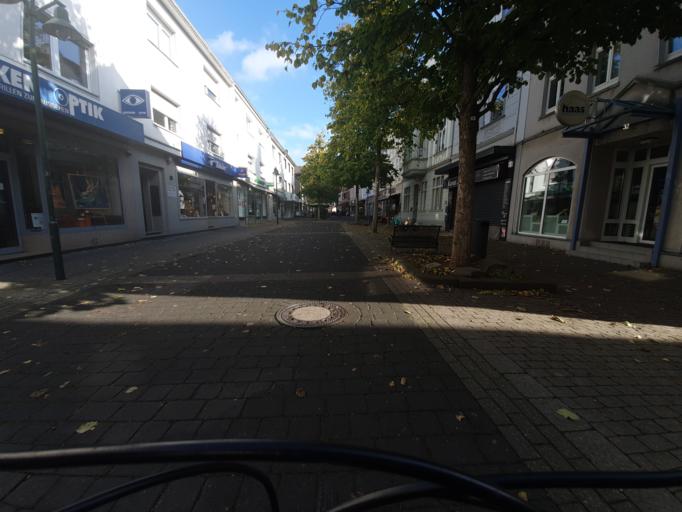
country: DE
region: North Rhine-Westphalia
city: Opladen
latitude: 51.0339
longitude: 7.0491
